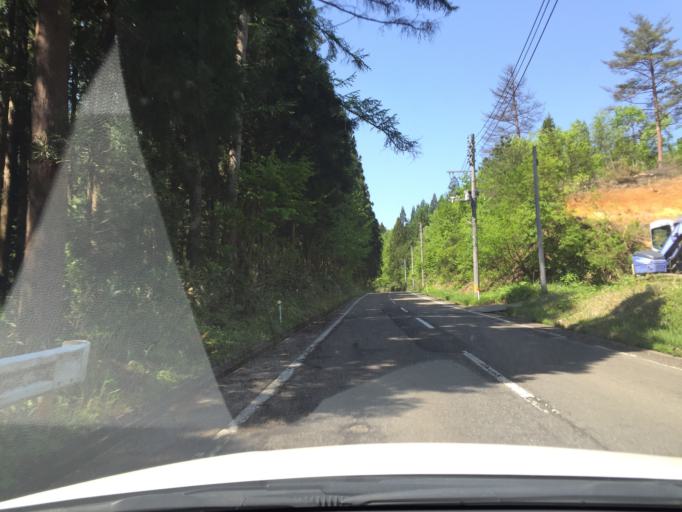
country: JP
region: Niigata
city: Kamo
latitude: 37.5608
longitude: 139.0824
